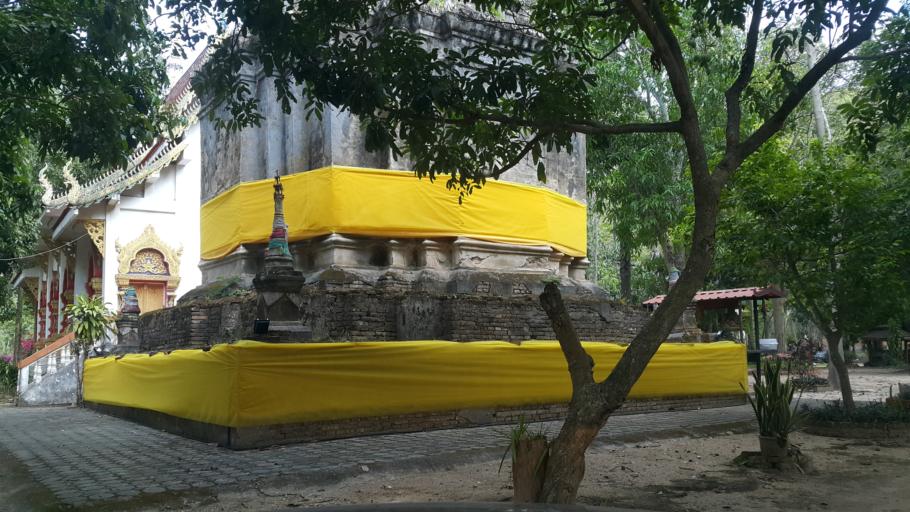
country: TH
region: Chiang Mai
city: Mae On
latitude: 18.7200
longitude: 99.2275
